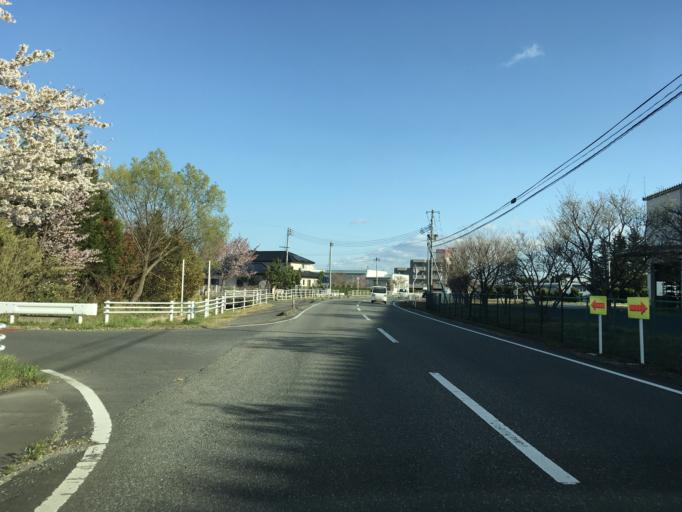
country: JP
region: Miyagi
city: Wakuya
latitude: 38.6714
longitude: 141.1934
